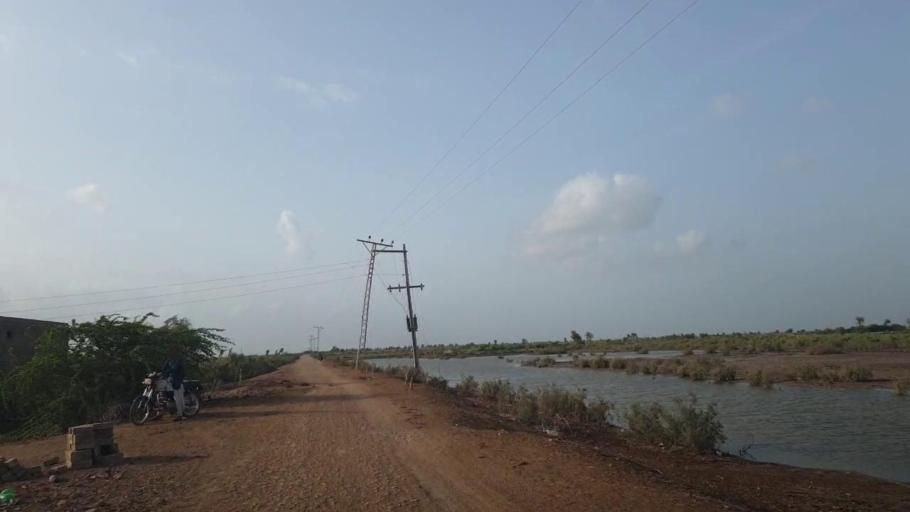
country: PK
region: Sindh
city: Tando Bago
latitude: 24.6517
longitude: 69.1119
